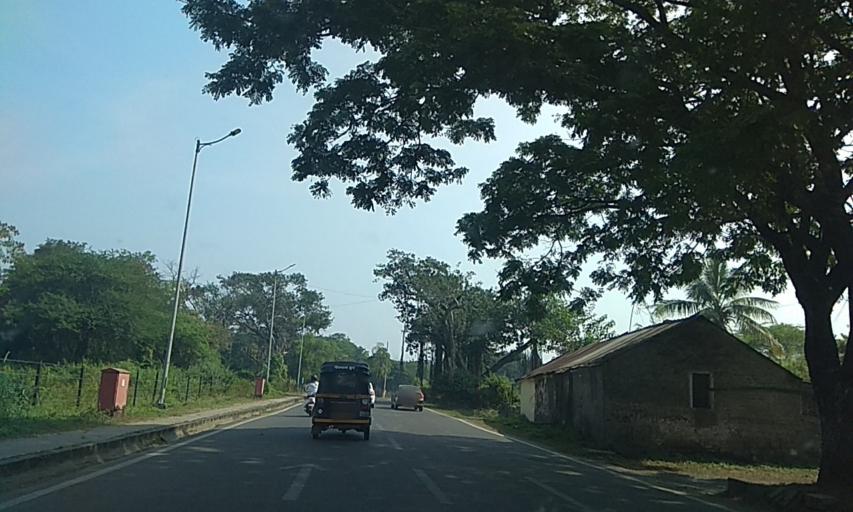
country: IN
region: Maharashtra
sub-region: Pune Division
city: Khadki
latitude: 18.5565
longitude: 73.8472
